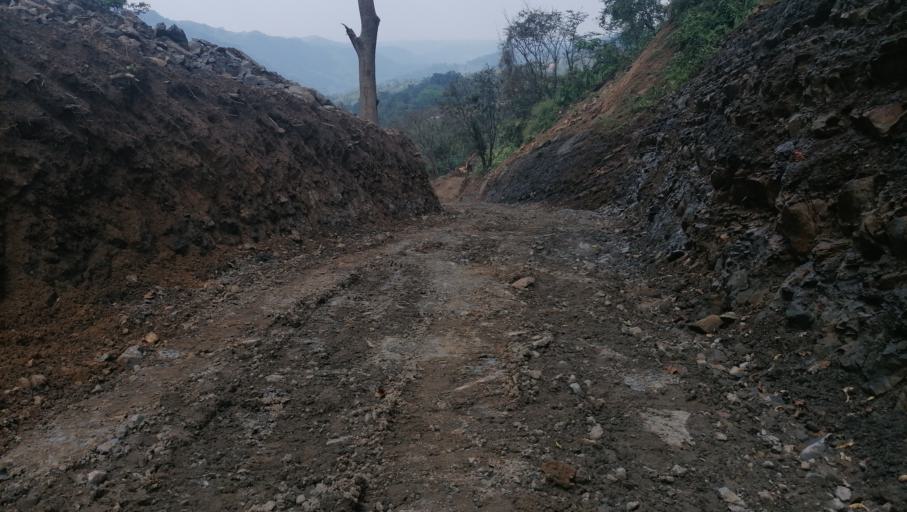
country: MX
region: Chiapas
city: Ostuacan
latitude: 17.3585
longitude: -93.3231
